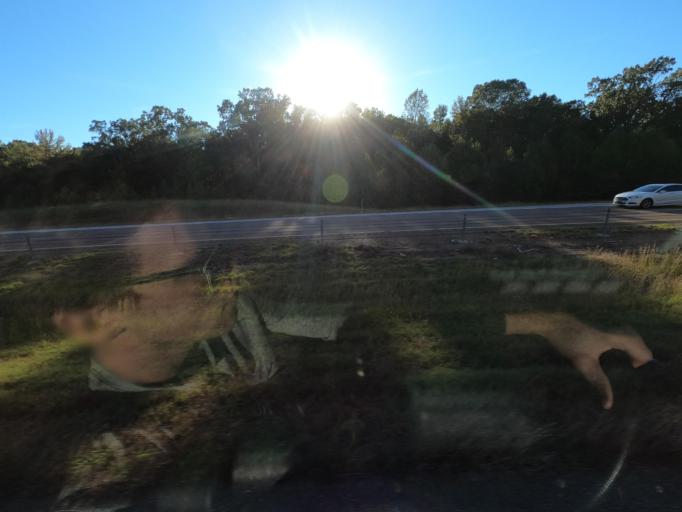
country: US
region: Tennessee
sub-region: Shelby County
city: Arlington
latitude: 35.2422
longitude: -89.6667
